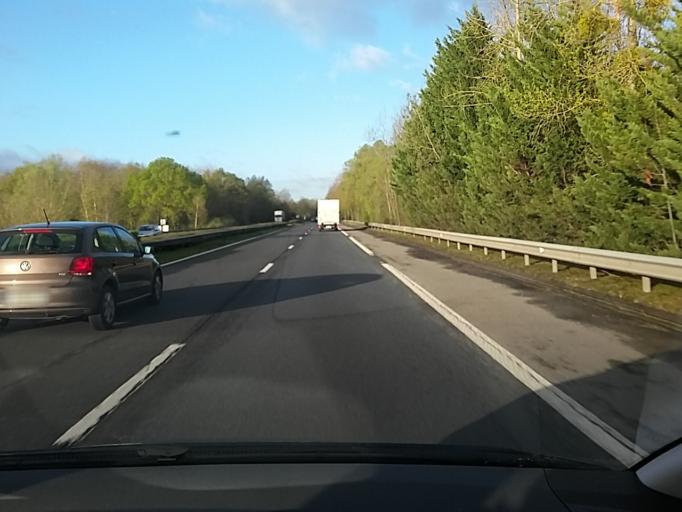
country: FR
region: Picardie
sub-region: Departement de l'Oise
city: Verberie
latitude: 49.3305
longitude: 2.7179
